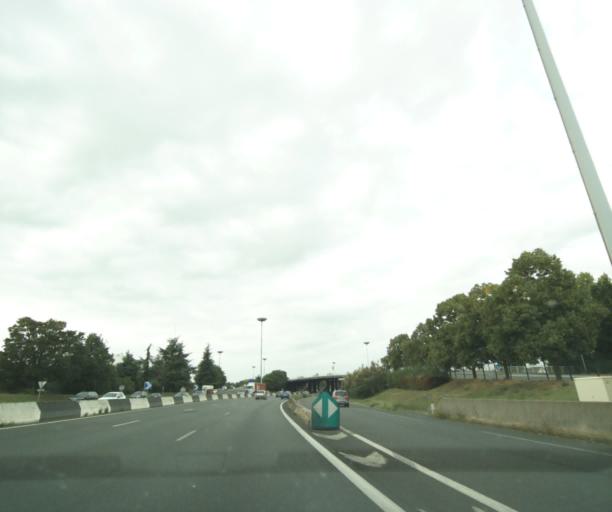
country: FR
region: Centre
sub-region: Departement d'Indre-et-Loire
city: Tours
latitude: 47.3915
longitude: 0.7063
